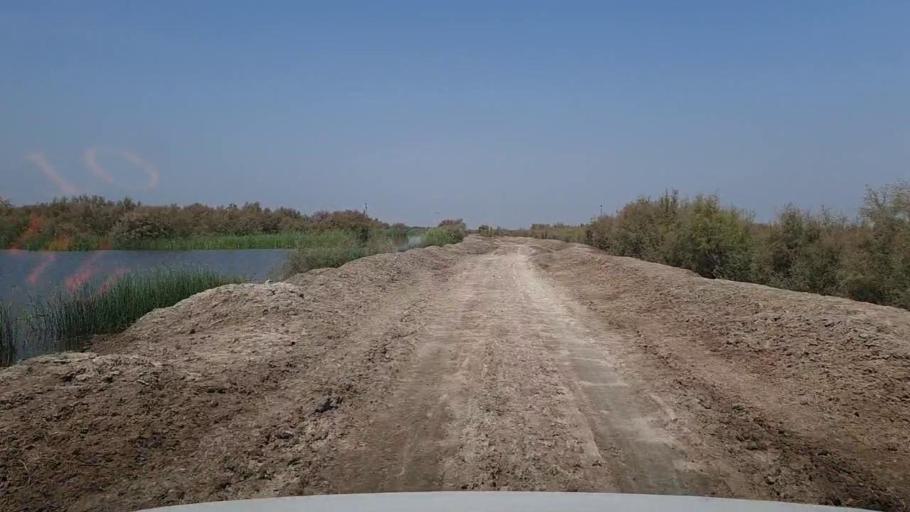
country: PK
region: Sindh
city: Kandhkot
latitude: 28.3436
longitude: 69.3020
